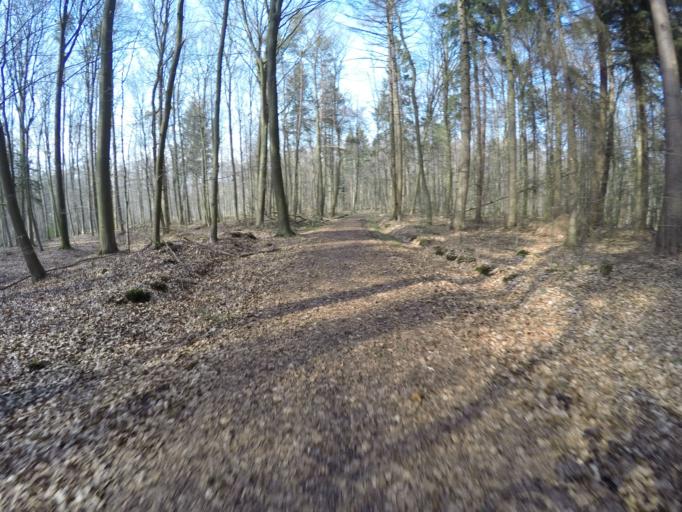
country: DE
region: Schleswig-Holstein
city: Borstel-Hohenraden
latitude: 53.7210
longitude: 9.8254
